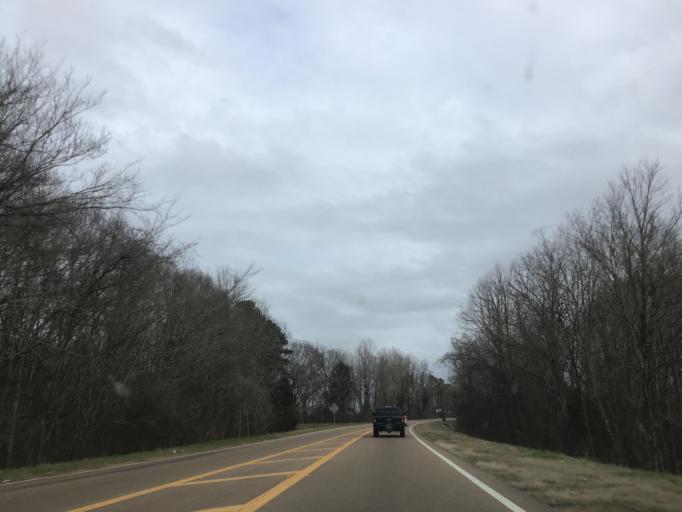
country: US
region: Mississippi
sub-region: Warren County
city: Beechwood
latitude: 32.3308
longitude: -90.8200
